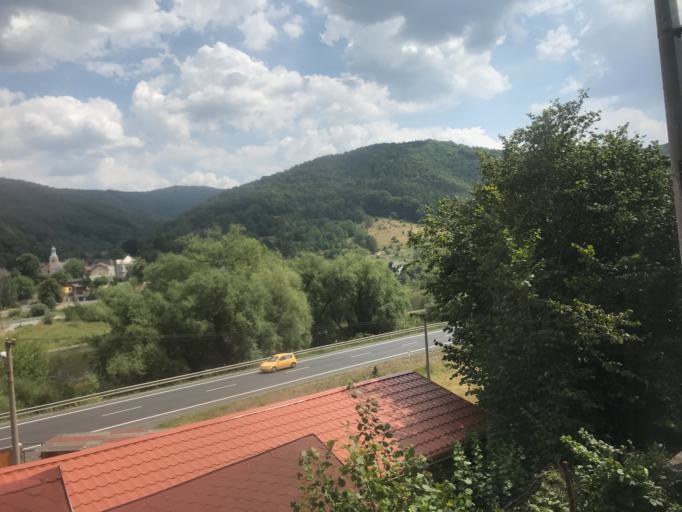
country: CZ
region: Ustecky
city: Povrly
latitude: 50.6971
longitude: 14.1982
